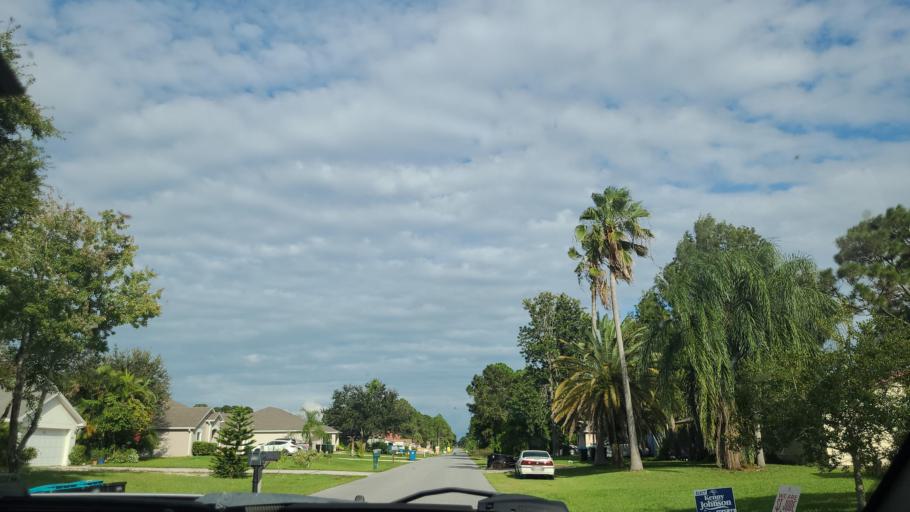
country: US
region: Florida
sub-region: Brevard County
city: Palm Bay
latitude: 27.9837
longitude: -80.6581
